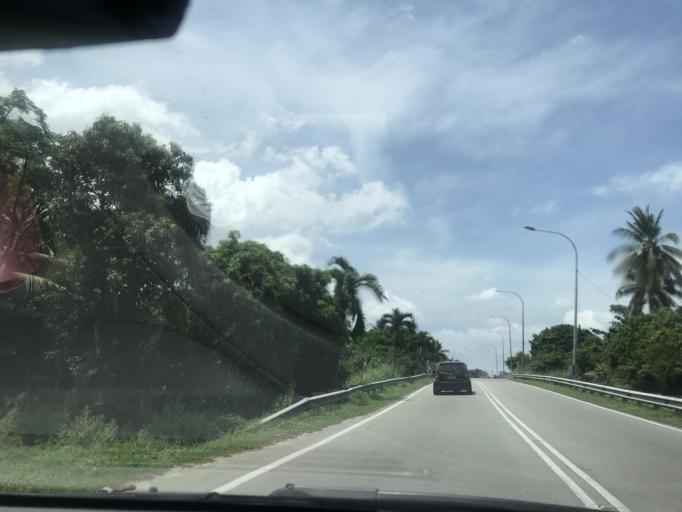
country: MY
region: Kelantan
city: Kota Bharu
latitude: 6.1539
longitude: 102.2046
